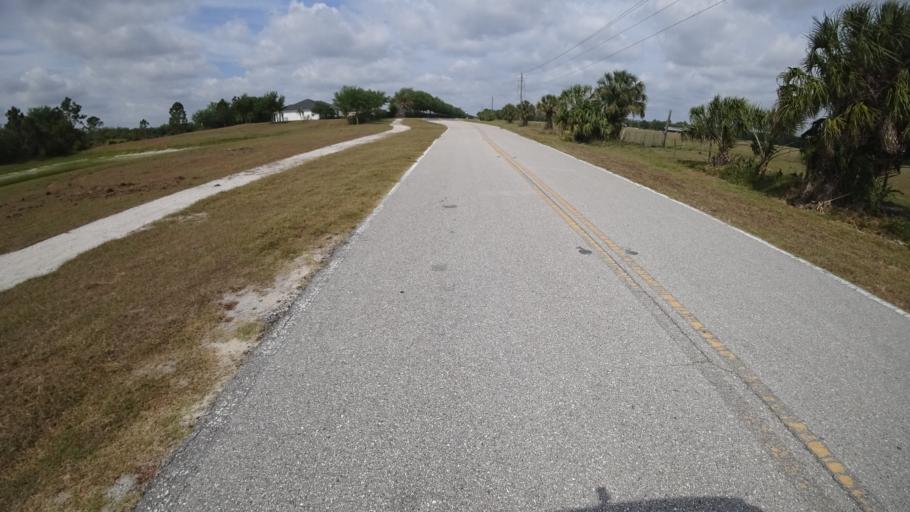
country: US
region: Florida
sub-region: Manatee County
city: Ellenton
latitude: 27.5355
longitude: -82.4020
